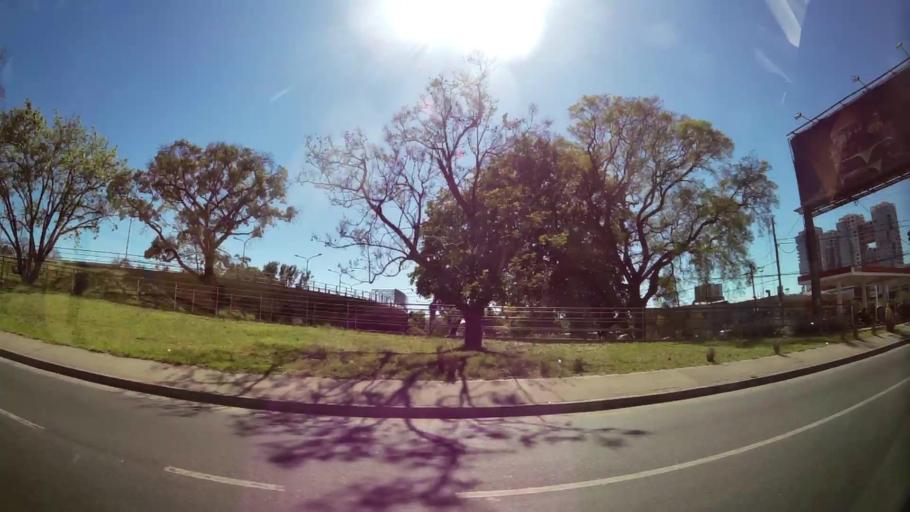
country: AR
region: Buenos Aires
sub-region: Partido de Vicente Lopez
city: Olivos
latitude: -34.5314
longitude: -58.4692
